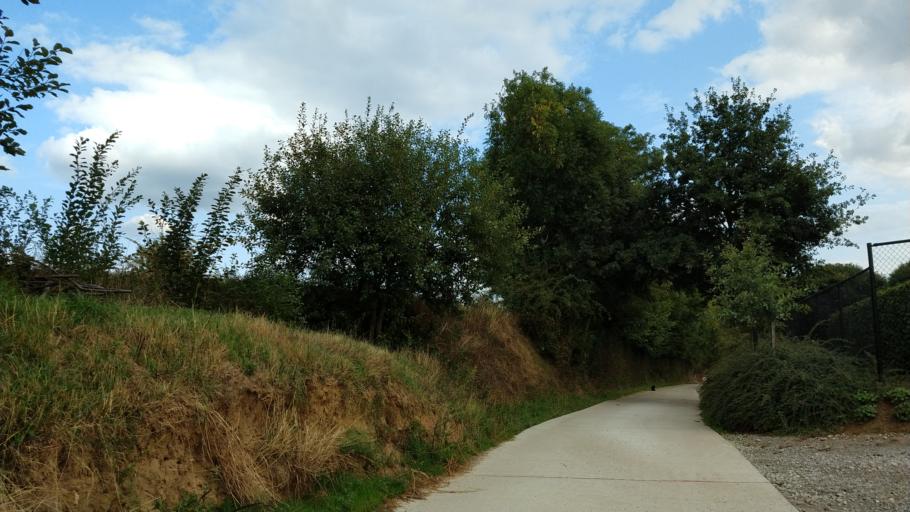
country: BE
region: Flanders
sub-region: Provincie Vlaams-Brabant
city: Boutersem
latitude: 50.8206
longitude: 4.8741
